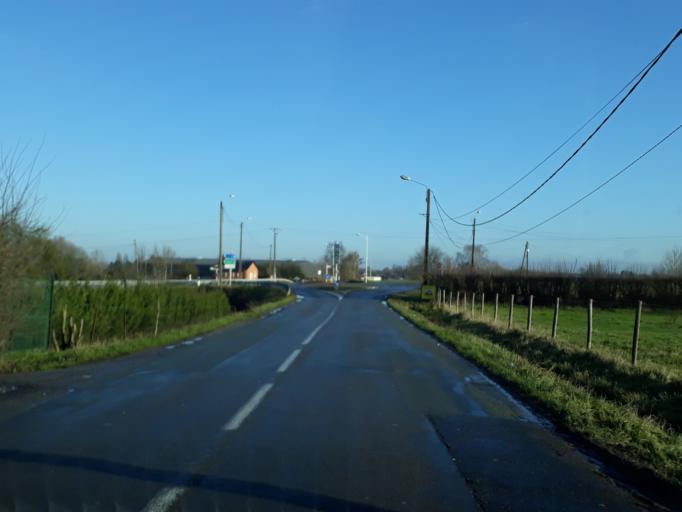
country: FR
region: Nord-Pas-de-Calais
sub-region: Departement du Nord
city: Wargnies-le-Grand
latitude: 50.3032
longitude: 3.6492
